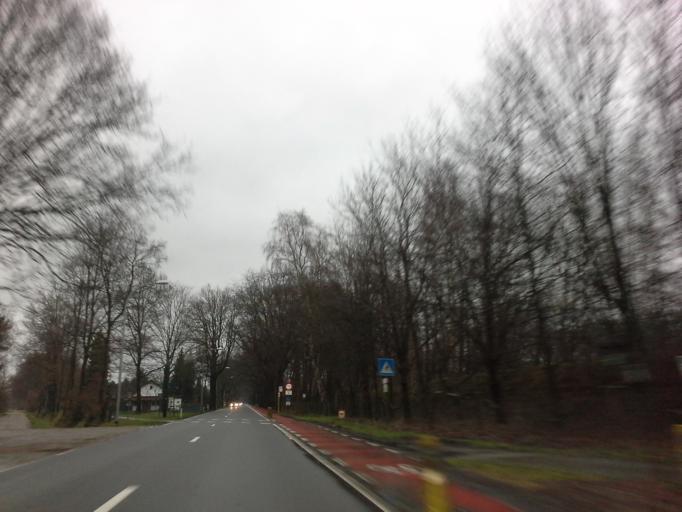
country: BE
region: Flanders
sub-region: Provincie Antwerpen
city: Baarle-Hertog
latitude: 51.3814
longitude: 4.9362
